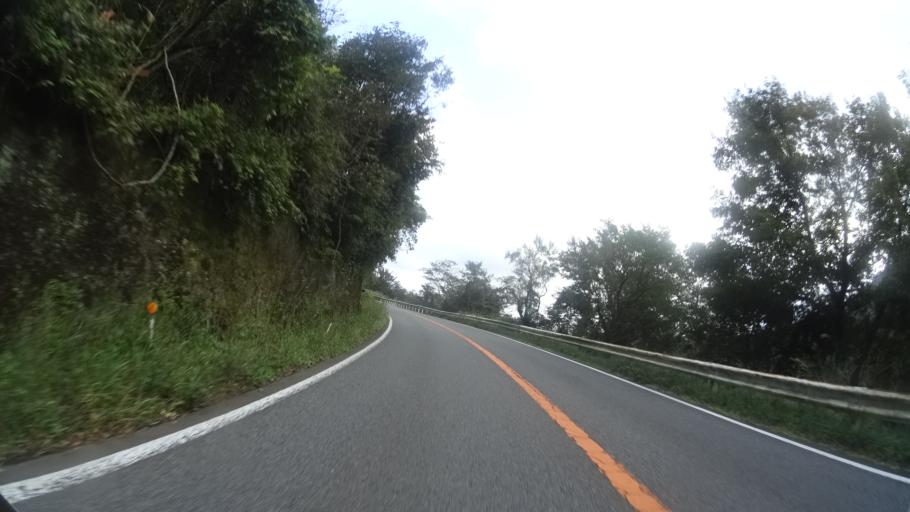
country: JP
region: Oita
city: Beppu
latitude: 33.2696
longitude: 131.4169
